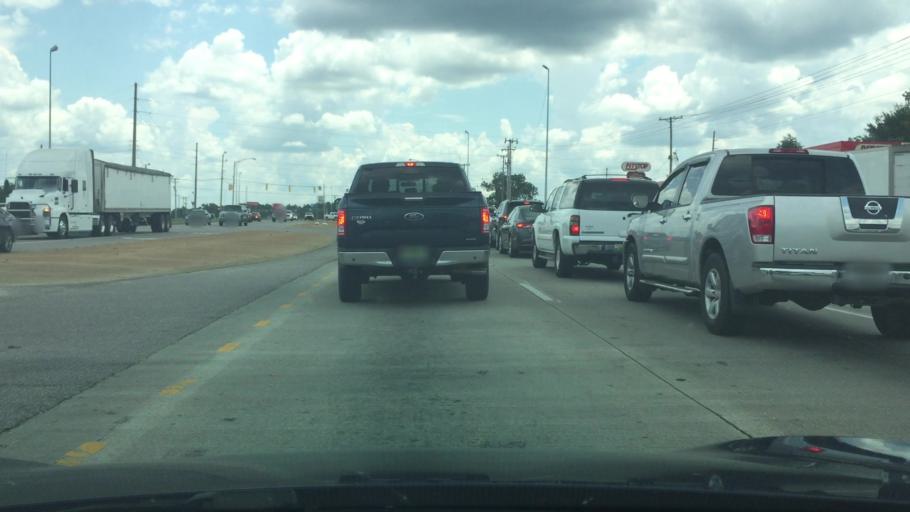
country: US
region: Alabama
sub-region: Pike County
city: Troy
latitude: 31.7933
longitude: -85.9789
